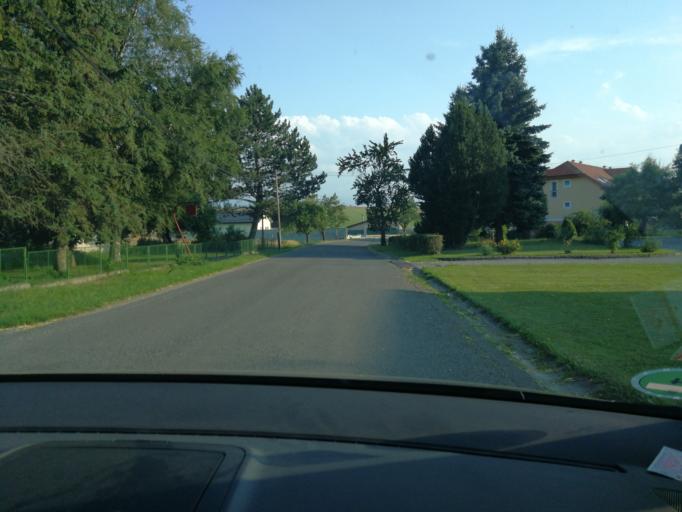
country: SK
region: Zilinsky
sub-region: Okres Liptovsky Mikulas
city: Liptovsky Mikulas
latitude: 49.1626
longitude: 19.5395
